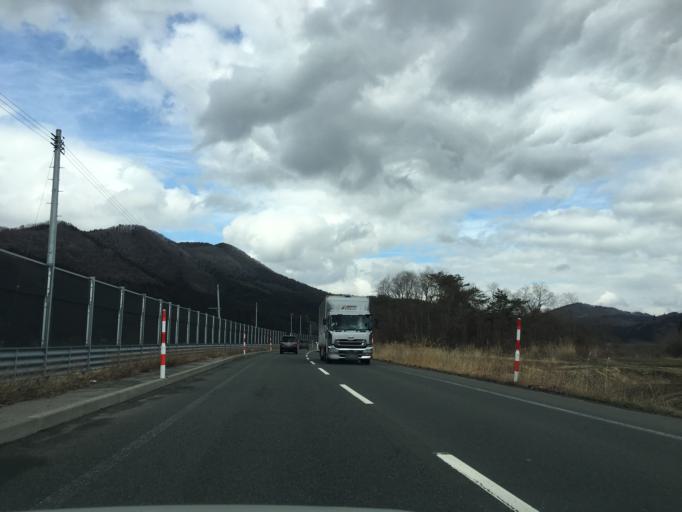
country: JP
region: Akita
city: Hanawa
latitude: 40.2279
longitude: 140.6798
